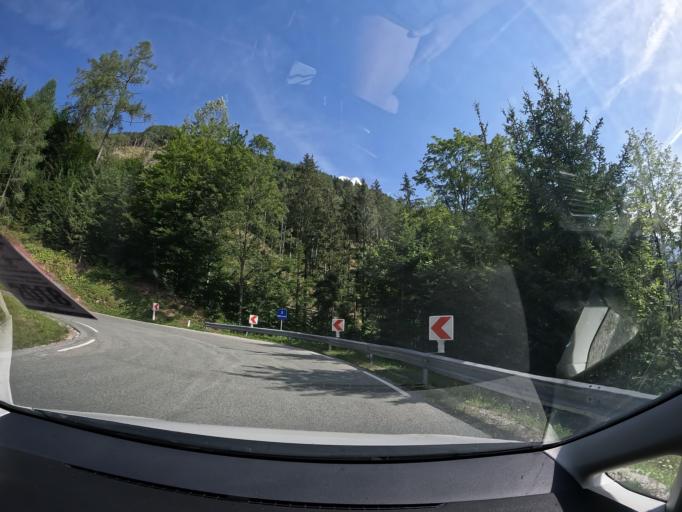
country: AT
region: Carinthia
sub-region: Politischer Bezirk Feldkirchen
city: Glanegg
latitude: 46.7226
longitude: 14.2458
